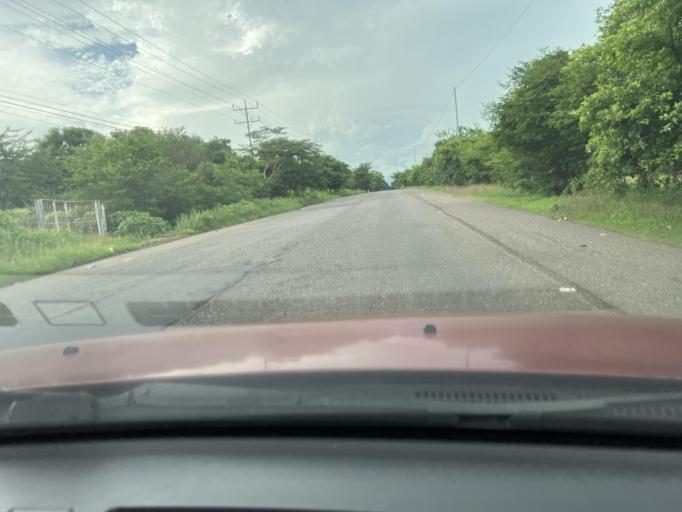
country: SV
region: La Union
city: San Alejo
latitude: 13.4138
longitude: -87.8893
